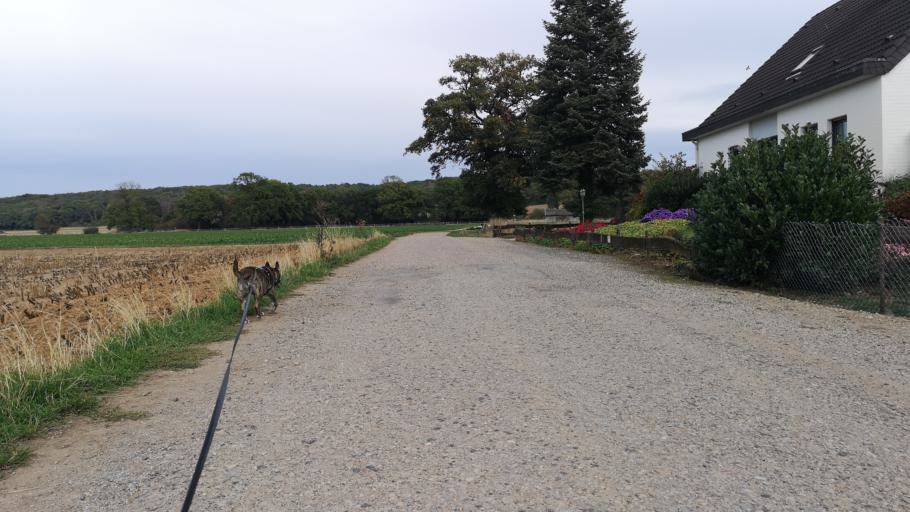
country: DE
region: North Rhine-Westphalia
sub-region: Regierungsbezirk Koln
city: Kreuzau
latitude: 50.7500
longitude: 6.4967
